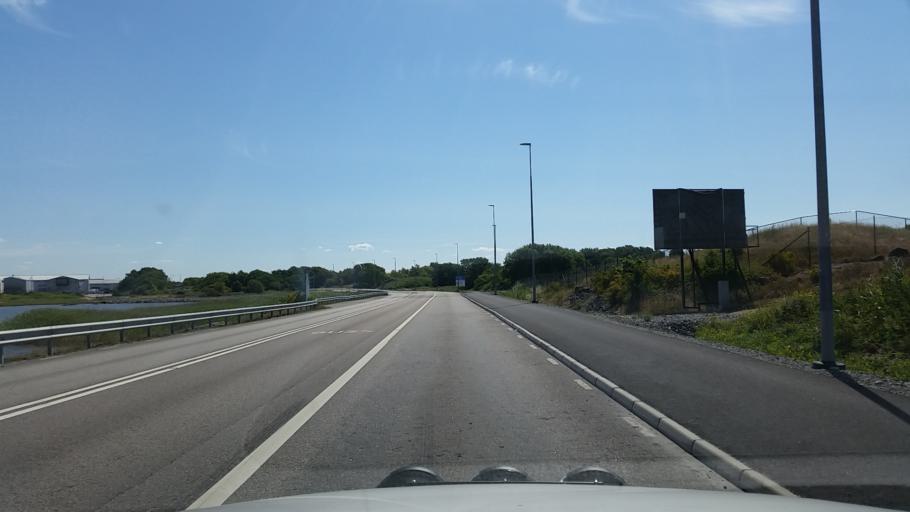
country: SE
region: Vaestra Goetaland
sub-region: Ockero Kommun
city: Hono
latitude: 57.6986
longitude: 11.6532
